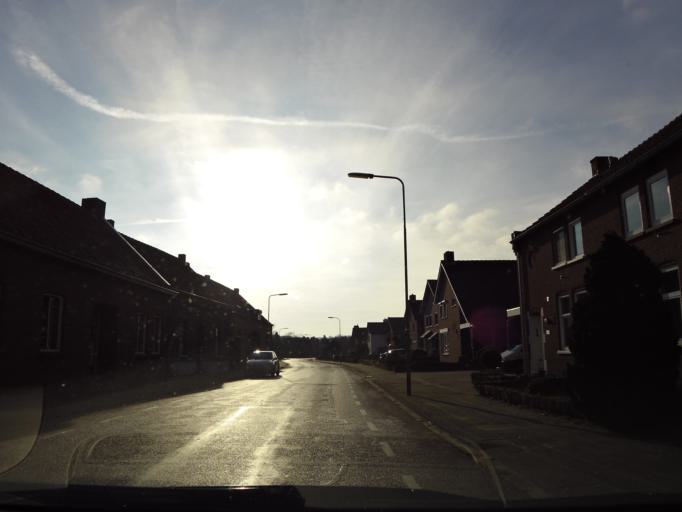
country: NL
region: Limburg
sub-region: Gemeente Beesel
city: Beesel
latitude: 51.2657
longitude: 6.0383
